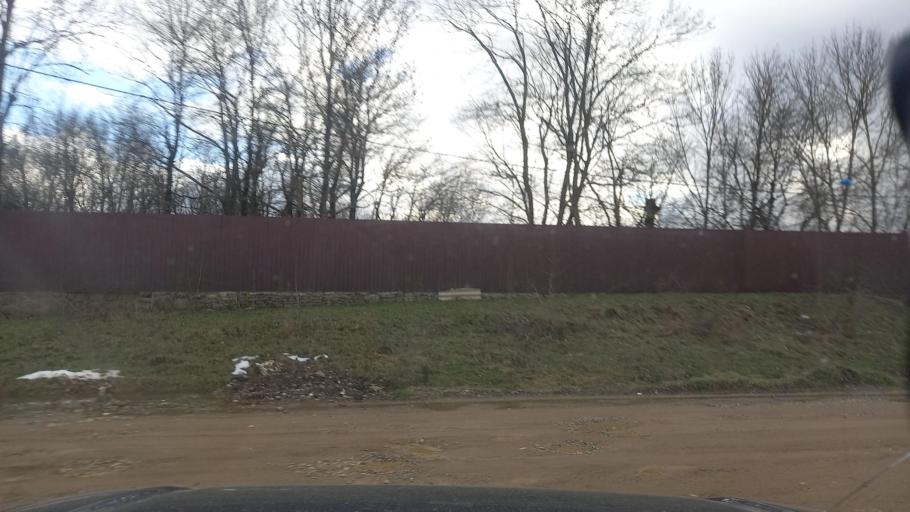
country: RU
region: Krasnodarskiy
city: Smolenskaya
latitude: 44.5659
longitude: 38.8043
